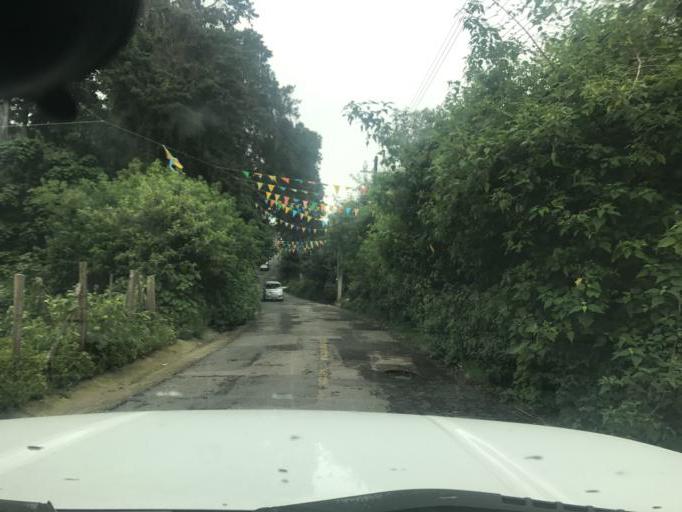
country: MX
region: Morelos
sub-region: Ocuituco
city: Huepalcalco (San Miguel)
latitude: 18.9029
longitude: -98.7514
